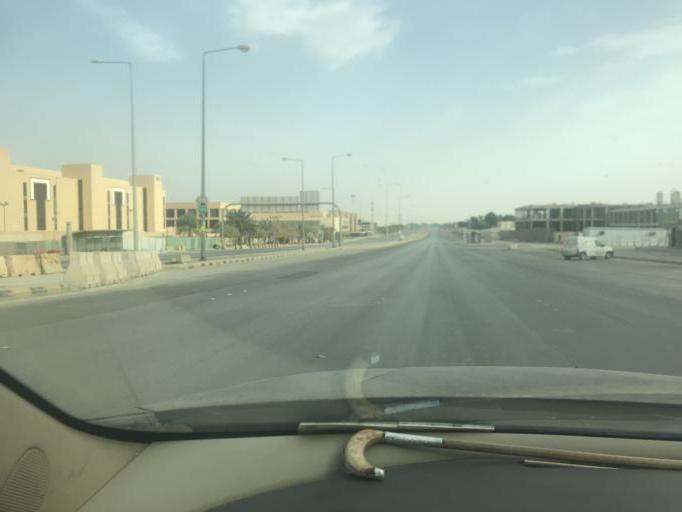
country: SA
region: Ar Riyad
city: Riyadh
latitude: 24.8147
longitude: 46.6892
